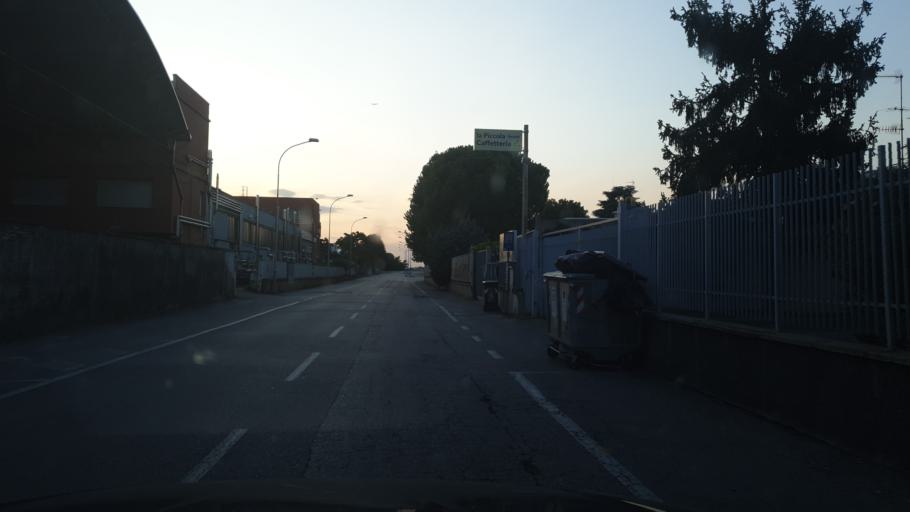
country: IT
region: Emilia-Romagna
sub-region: Provincia di Bologna
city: Quarto Inferiore
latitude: 44.5499
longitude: 11.3907
